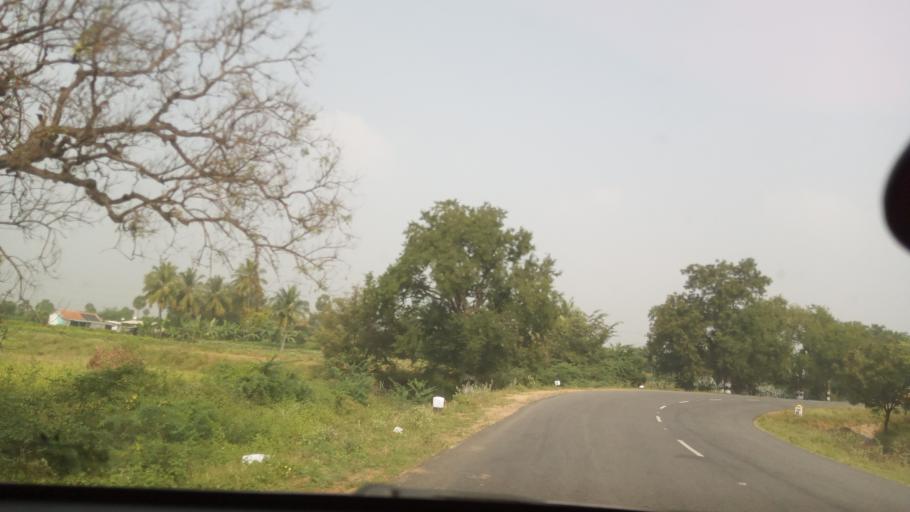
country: IN
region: Tamil Nadu
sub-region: Erode
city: Punjai Puliyampatti
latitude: 11.3901
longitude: 77.1779
